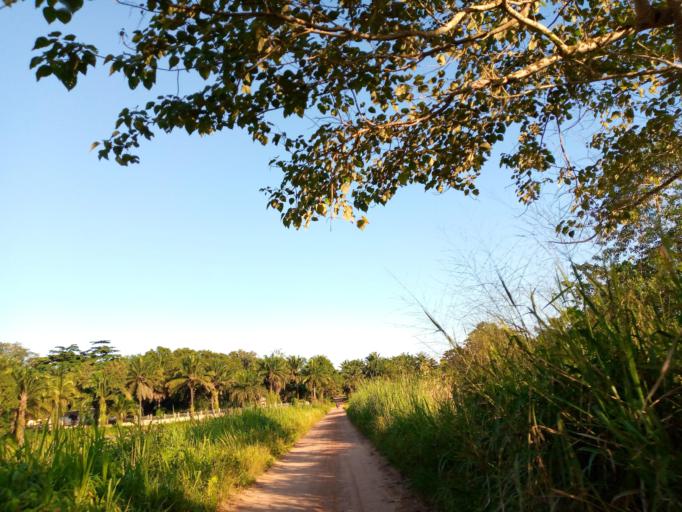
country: SL
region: Northern Province
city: Yonibana
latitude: 8.4484
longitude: -12.2424
